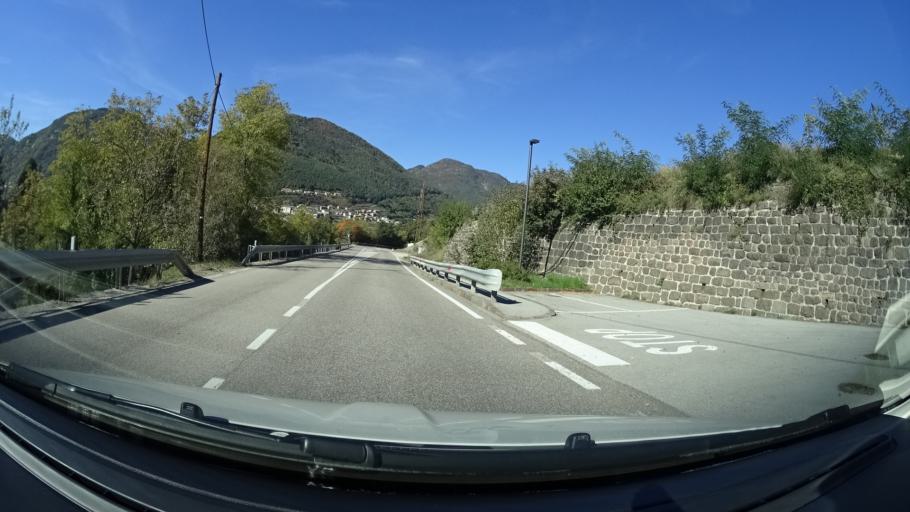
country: IT
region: Trentino-Alto Adige
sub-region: Provincia di Trento
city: Faver
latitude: 46.1733
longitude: 11.2484
